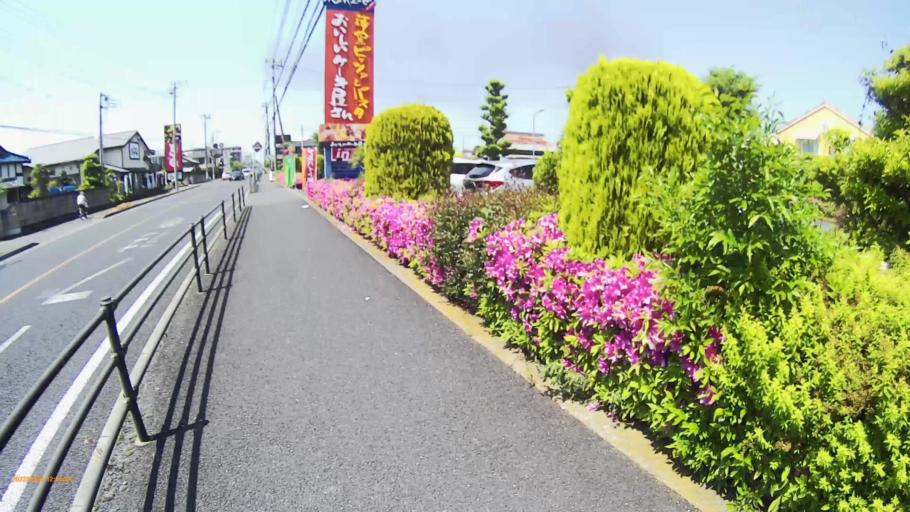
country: JP
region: Saitama
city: Kasukabe
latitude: 35.9569
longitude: 139.7760
